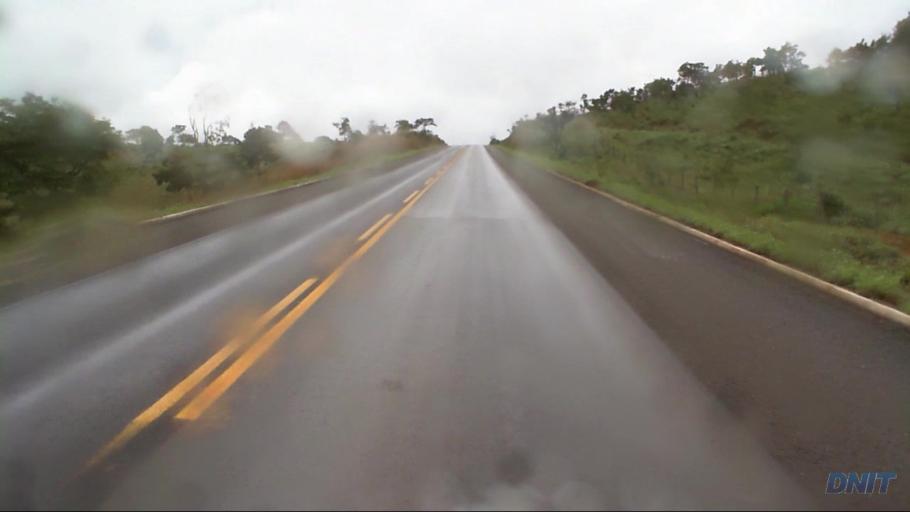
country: BR
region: Goias
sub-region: Padre Bernardo
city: Padre Bernardo
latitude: -15.2010
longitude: -48.4538
